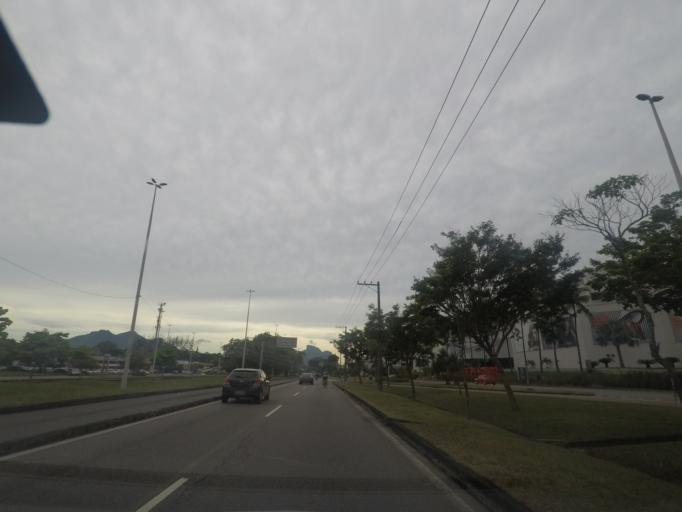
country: BR
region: Rio de Janeiro
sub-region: Nilopolis
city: Nilopolis
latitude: -23.0006
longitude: -43.3871
